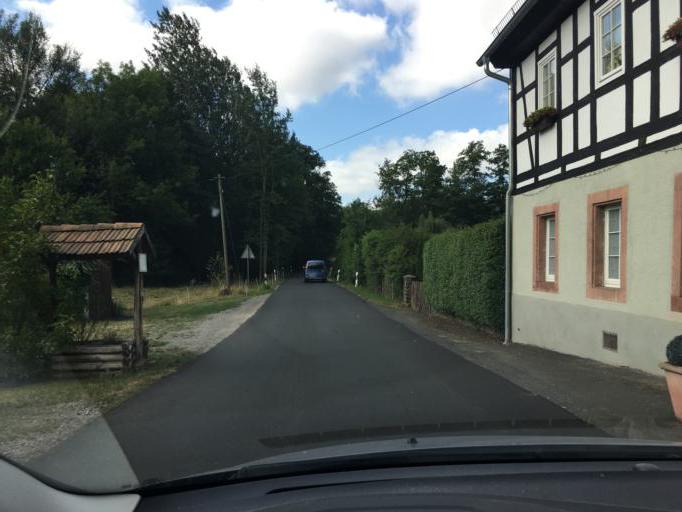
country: DE
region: Saxony
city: Frohburg
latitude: 51.0303
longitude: 12.6134
